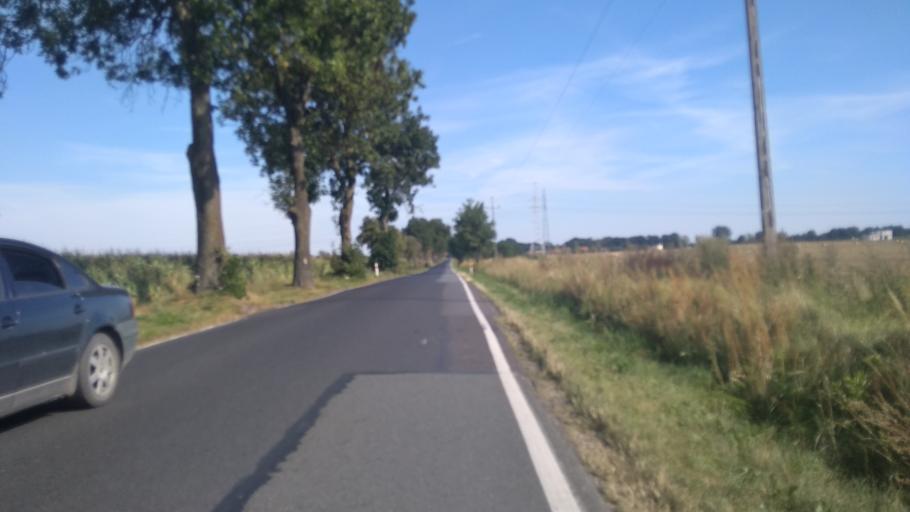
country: PL
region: Kujawsko-Pomorskie
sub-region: Powiat bydgoski
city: Osielsko
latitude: 53.2159
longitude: 18.1443
